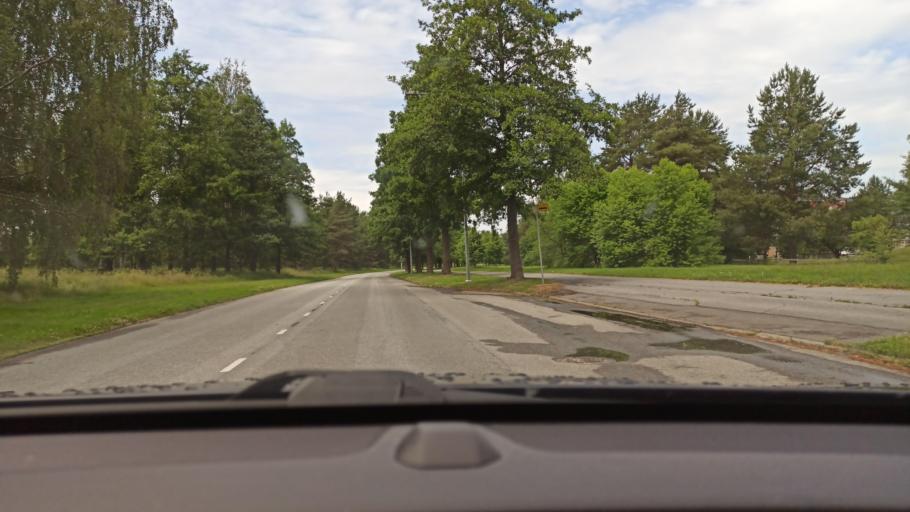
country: FI
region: Satakunta
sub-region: Pori
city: Pori
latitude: 61.5049
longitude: 21.7792
